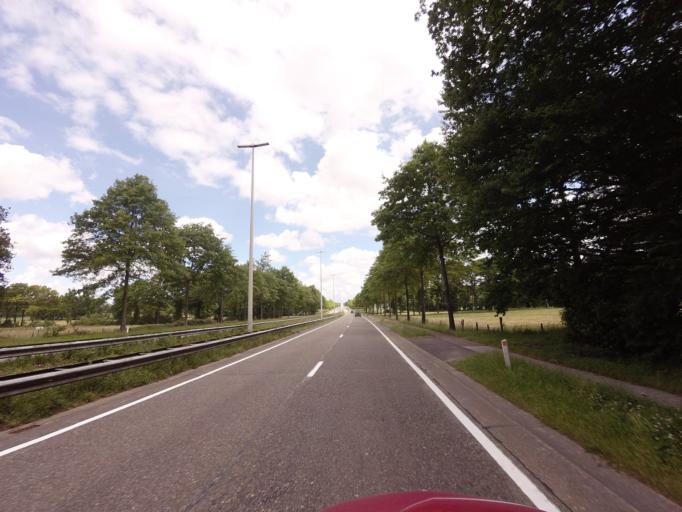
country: BE
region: Flanders
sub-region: Provincie Oost-Vlaanderen
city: Maldegem
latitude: 51.1734
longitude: 3.4468
